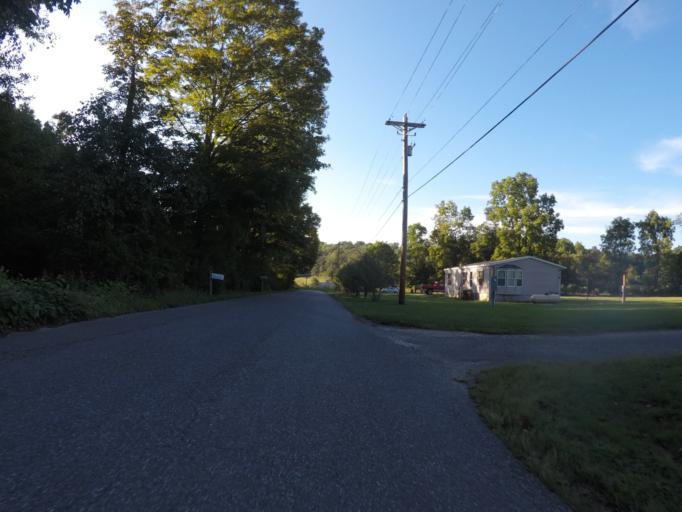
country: US
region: Ohio
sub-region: Lawrence County
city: Coal Grove
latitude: 38.5358
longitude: -82.5320
